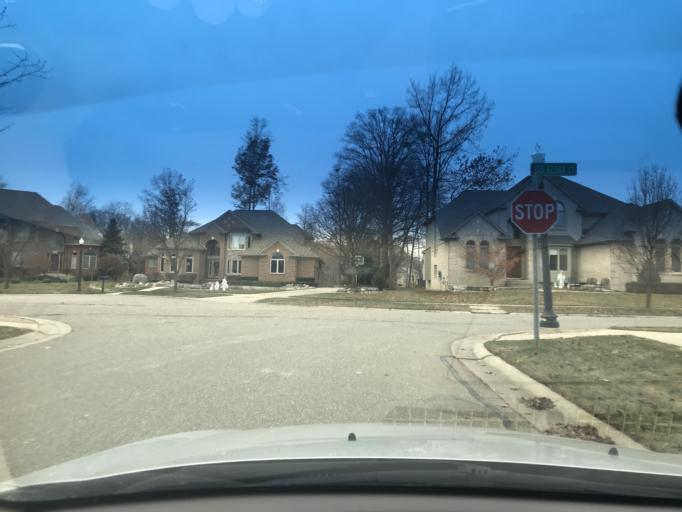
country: US
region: Michigan
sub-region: Macomb County
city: Shelby
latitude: 42.7066
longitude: -83.0402
